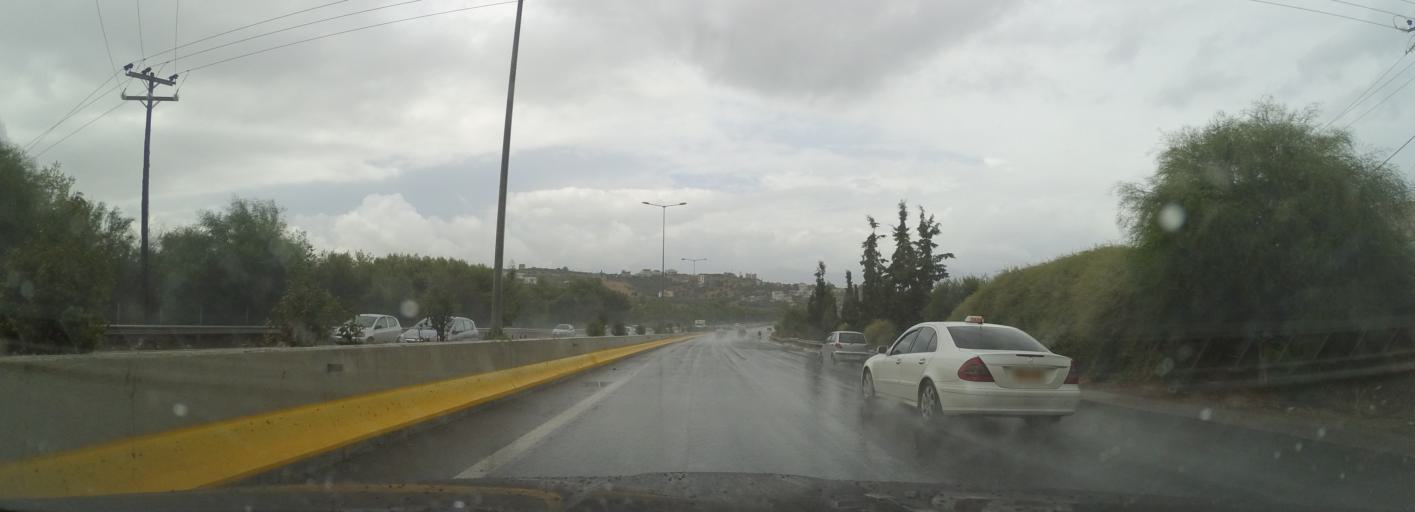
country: GR
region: Crete
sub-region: Nomos Irakleiou
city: Irakleion
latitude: 35.3174
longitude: 25.1302
